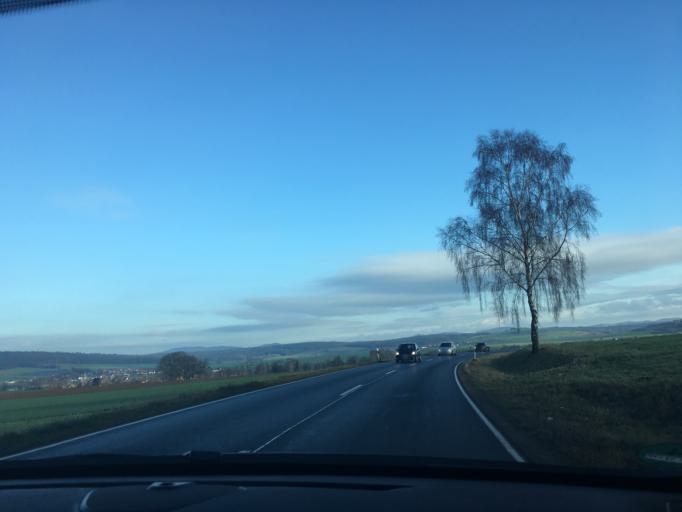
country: DE
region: Hesse
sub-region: Regierungsbezirk Kassel
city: Dipperz
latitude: 50.5742
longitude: 9.7780
